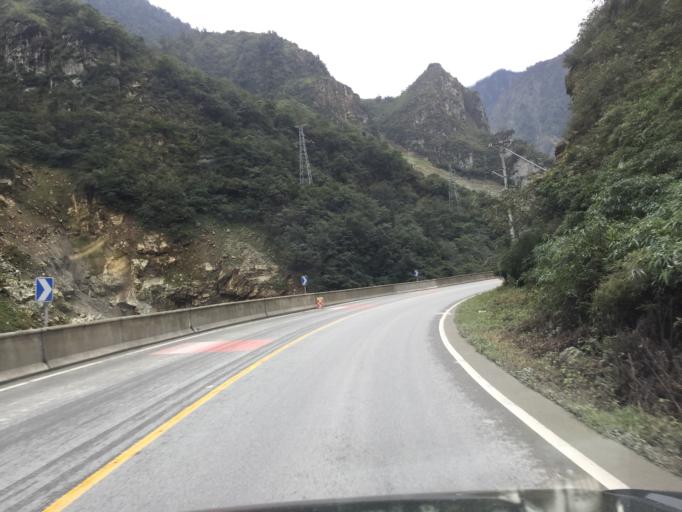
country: CN
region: Sichuan
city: Guangsheng
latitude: 31.0616
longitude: 103.4109
